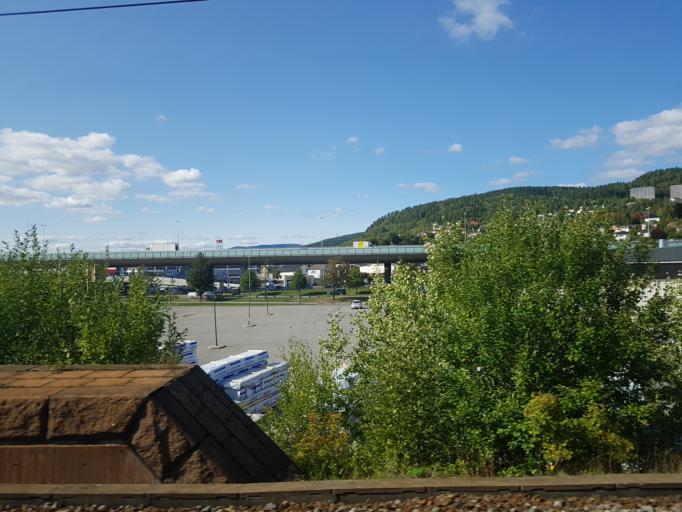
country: NO
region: Buskerud
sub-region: Drammen
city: Drammen
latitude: 59.7405
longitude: 10.2293
